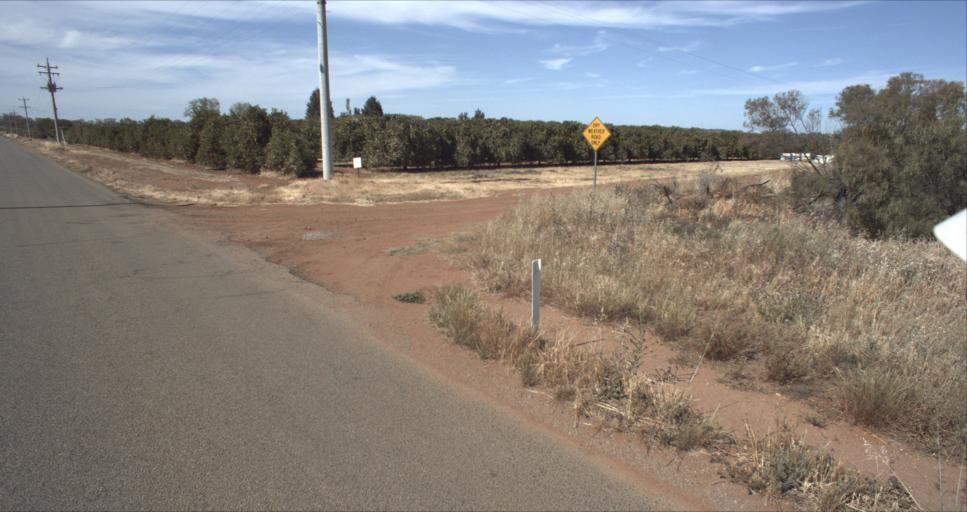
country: AU
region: New South Wales
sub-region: Leeton
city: Leeton
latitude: -34.5726
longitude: 146.4752
